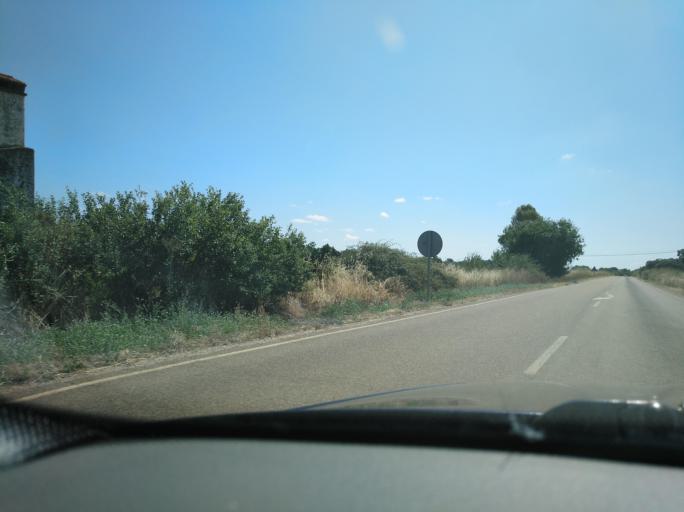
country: ES
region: Extremadura
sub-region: Provincia de Badajoz
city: Olivenza
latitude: 38.7213
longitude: -7.2083
